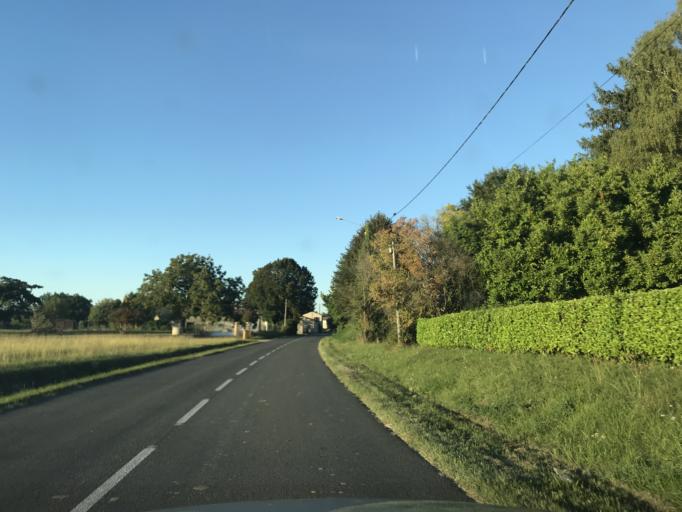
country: FR
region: Aquitaine
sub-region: Departement de la Gironde
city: Saint-Medard-de-Guizieres
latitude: 45.0023
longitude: -0.0535
